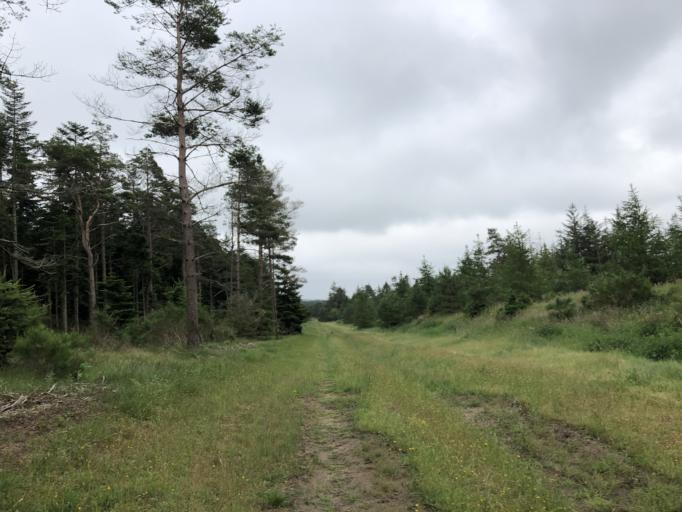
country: DK
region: Central Jutland
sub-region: Holstebro Kommune
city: Ulfborg
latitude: 56.2511
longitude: 8.3601
